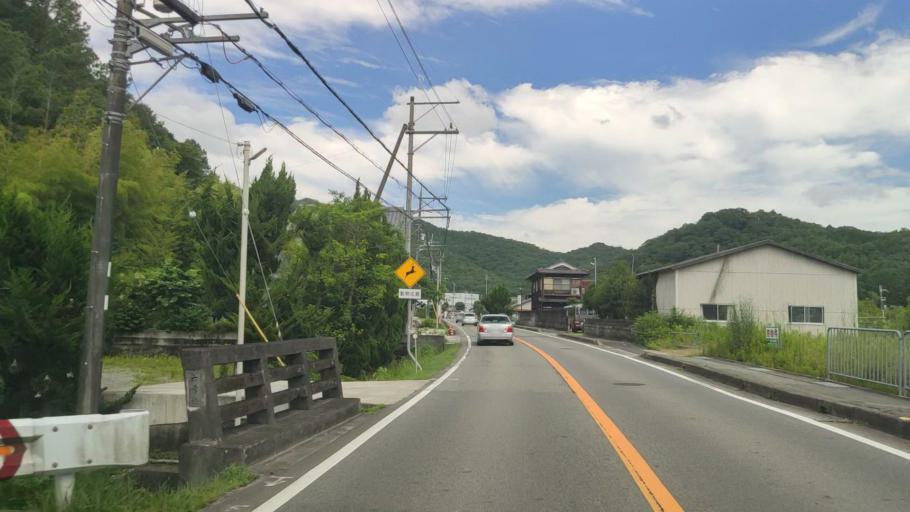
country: JP
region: Hyogo
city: Nishiwaki
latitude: 35.0212
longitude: 134.9481
